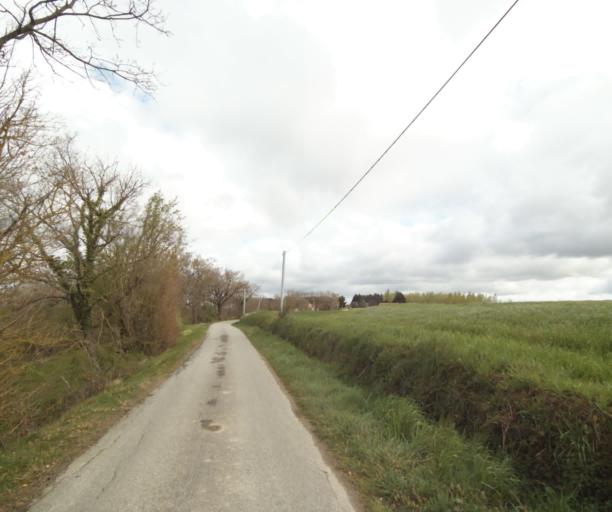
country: FR
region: Midi-Pyrenees
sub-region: Departement de l'Ariege
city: Saverdun
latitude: 43.2217
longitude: 1.5596
